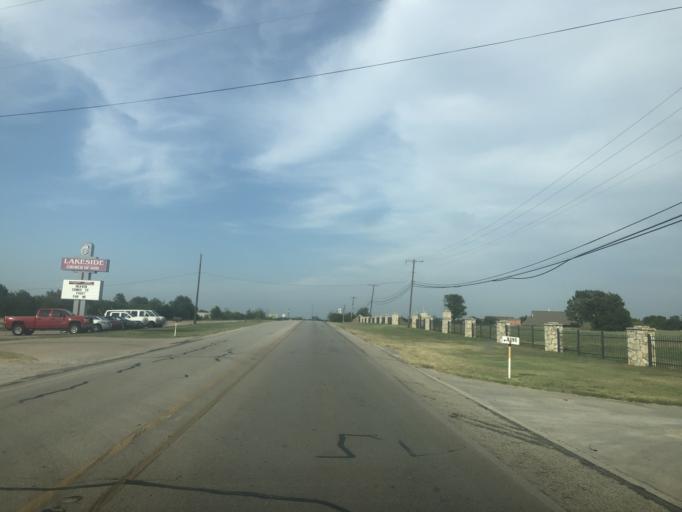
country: US
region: Texas
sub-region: Tarrant County
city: Lakeside
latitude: 32.8243
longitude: -97.4844
